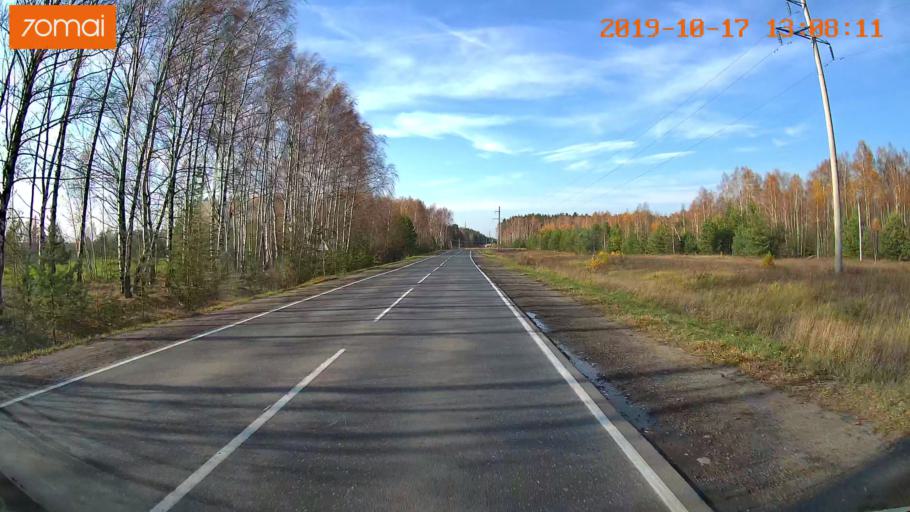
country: RU
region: Rjazan
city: Syntul
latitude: 54.9873
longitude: 41.2733
